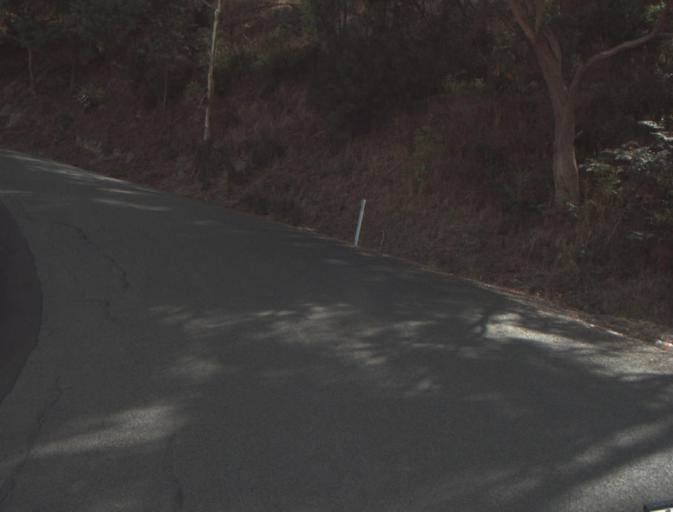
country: AU
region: Tasmania
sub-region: Launceston
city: Mayfield
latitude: -41.2460
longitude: 147.1514
